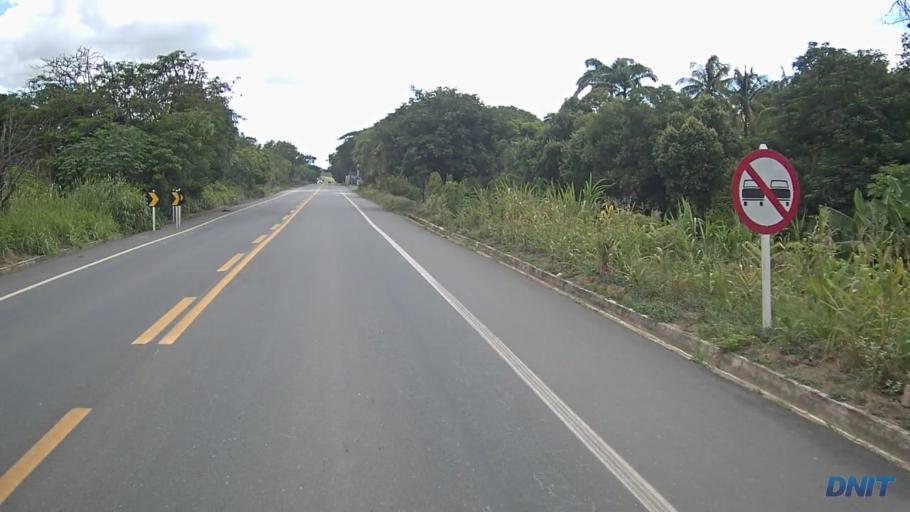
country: BR
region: Minas Gerais
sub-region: Governador Valadares
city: Governador Valadares
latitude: -18.9397
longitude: -42.0567
